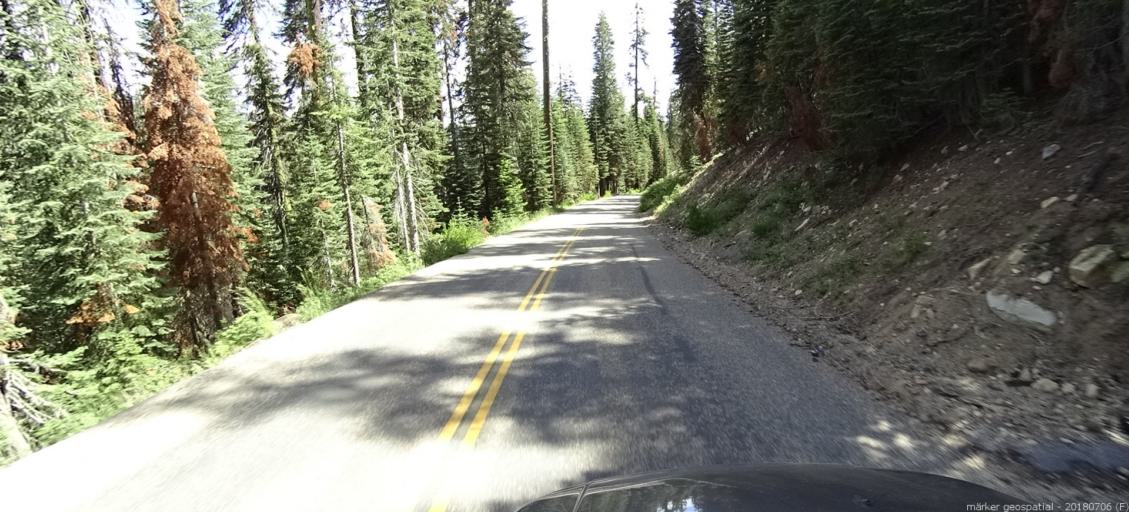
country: US
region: California
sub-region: Madera County
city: Oakhurst
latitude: 37.4281
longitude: -119.4866
